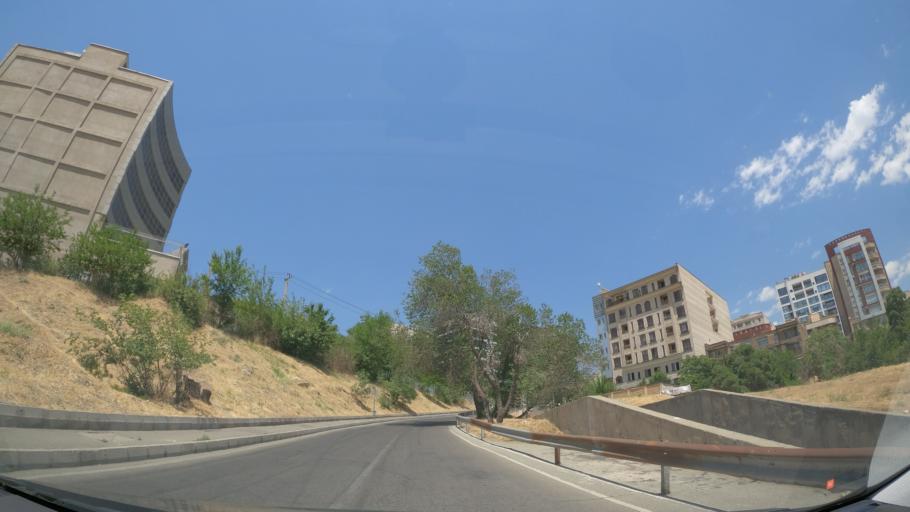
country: IR
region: Tehran
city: Tajrish
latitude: 35.7796
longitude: 51.3871
